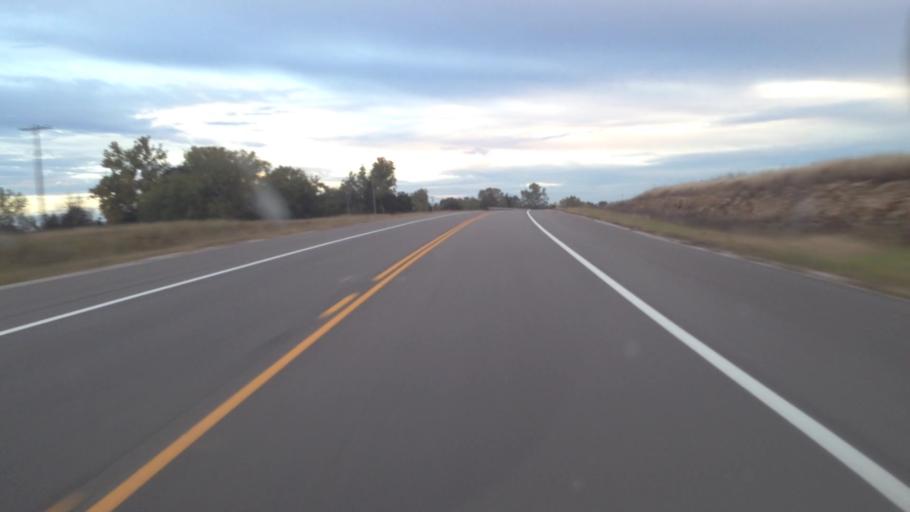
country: US
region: Kansas
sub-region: Anderson County
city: Garnett
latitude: 38.3311
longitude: -95.2490
